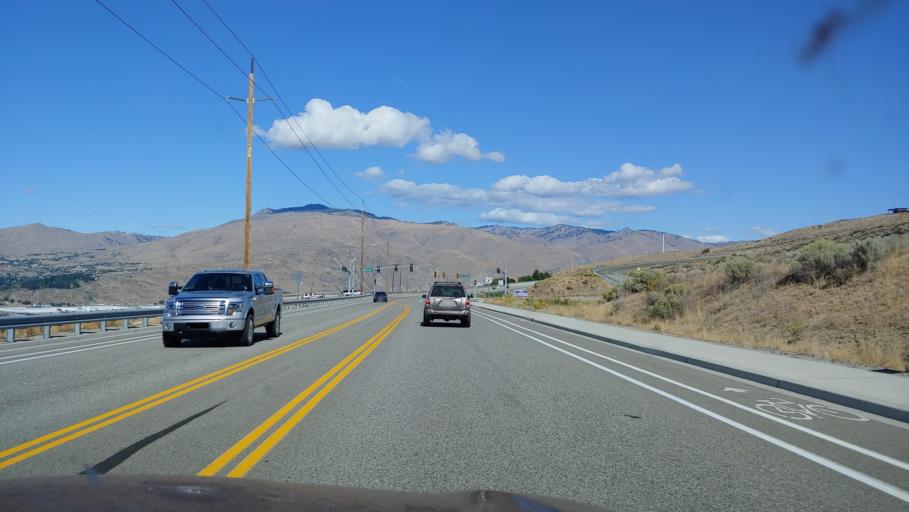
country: US
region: Washington
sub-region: Douglas County
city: East Wenatchee Bench
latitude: 47.4544
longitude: -120.2917
